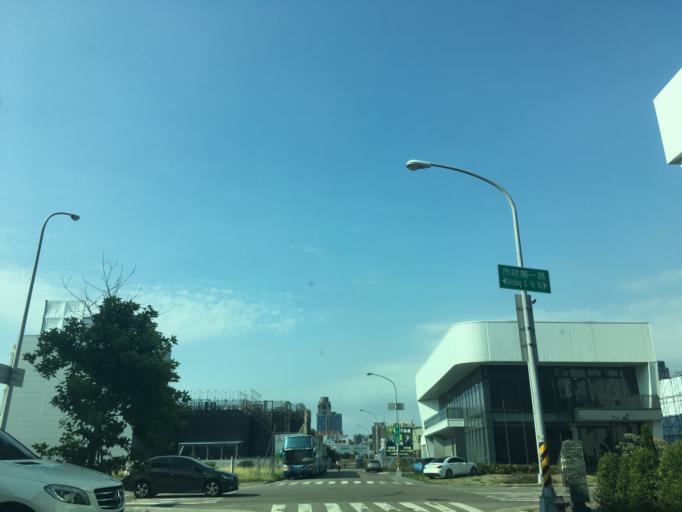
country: TW
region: Taiwan
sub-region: Taichung City
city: Taichung
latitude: 24.1589
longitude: 120.6284
